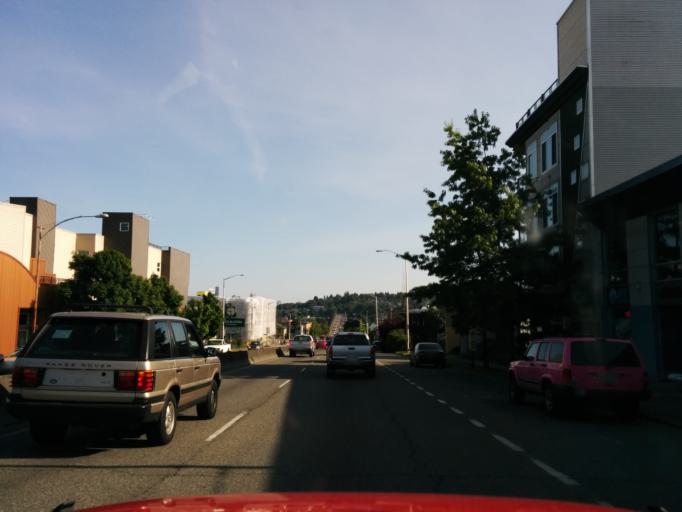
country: US
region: Washington
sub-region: King County
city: Seattle
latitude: 47.6566
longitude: -122.3474
